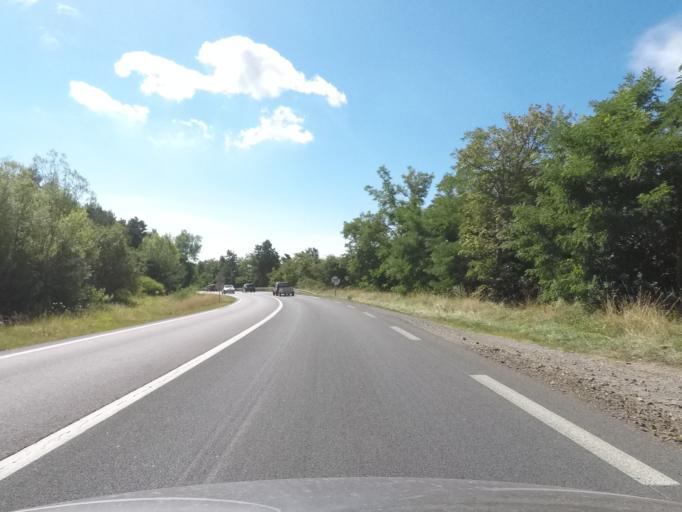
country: FR
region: Auvergne
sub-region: Departement du Puy-de-Dome
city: Ceyrat
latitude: 45.7084
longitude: 3.0594
